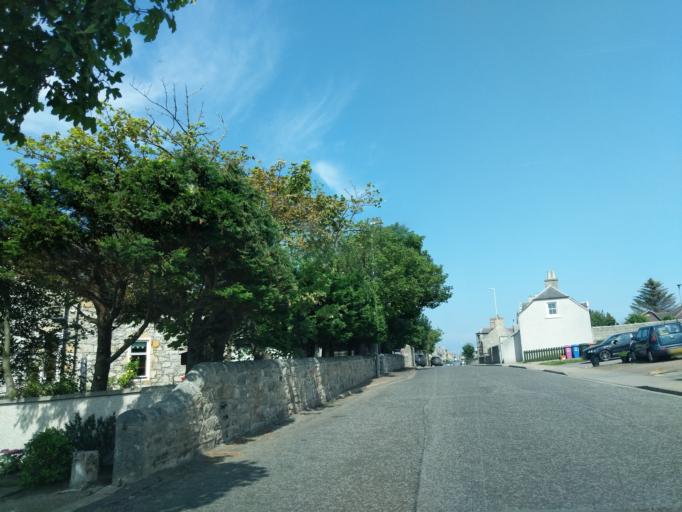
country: GB
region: Scotland
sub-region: Moray
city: Lossiemouth
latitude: 57.7183
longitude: -3.3007
